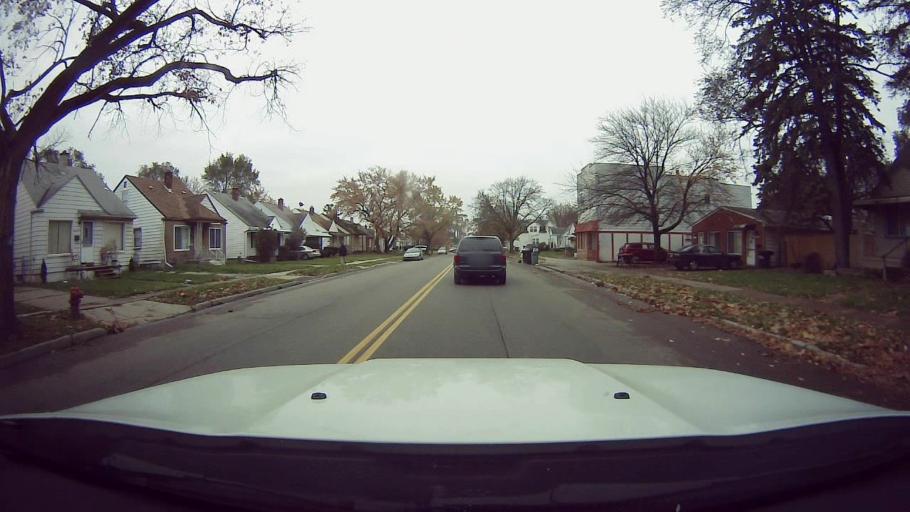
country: US
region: Michigan
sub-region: Wayne County
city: Dearborn Heights
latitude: 42.3414
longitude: -83.2354
